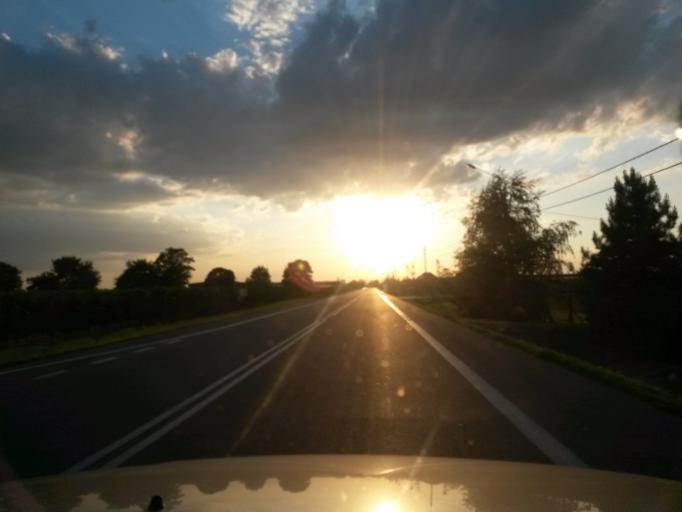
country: PL
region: Lodz Voivodeship
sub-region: Powiat wielunski
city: Czarnozyly
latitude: 51.2548
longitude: 18.4991
